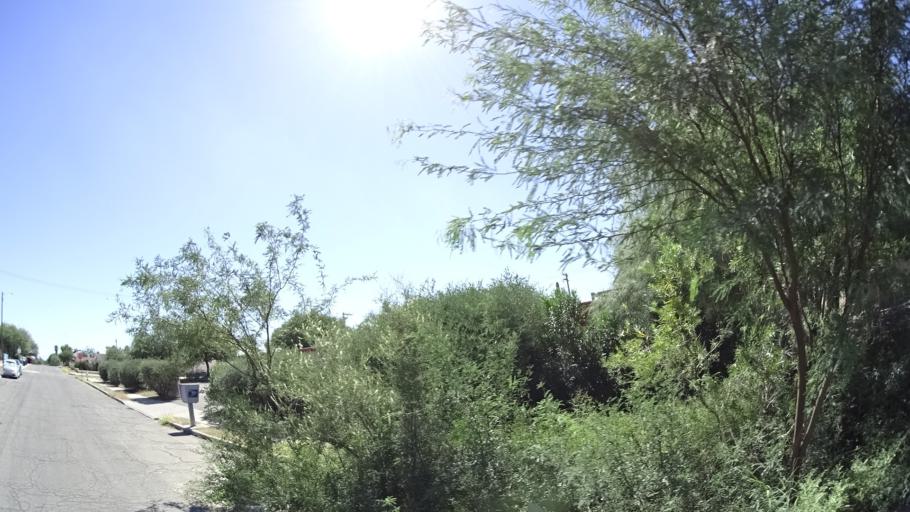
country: US
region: Arizona
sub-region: Pima County
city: Tucson
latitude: 32.2425
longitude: -110.9618
